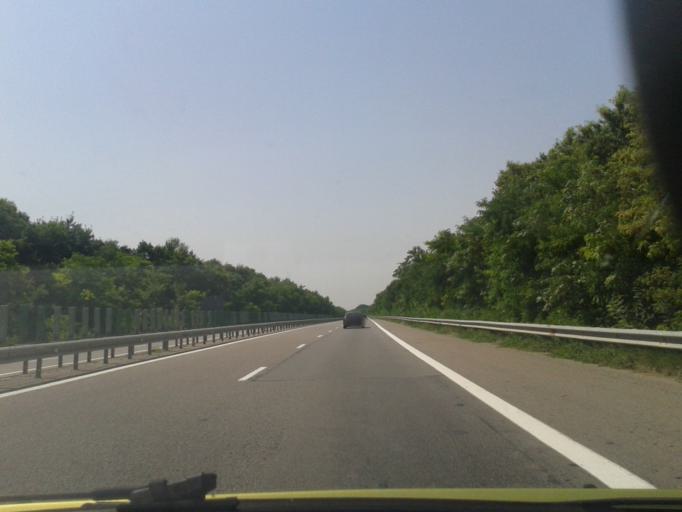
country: RO
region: Calarasi
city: Lehliu-Gara
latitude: 44.4313
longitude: 26.8378
